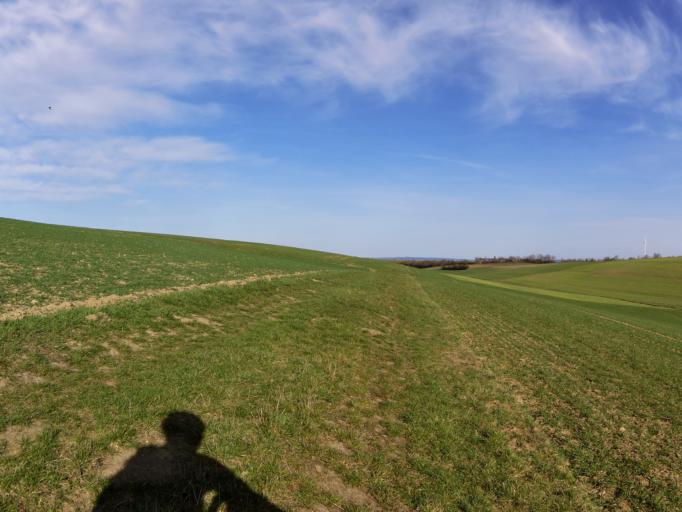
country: DE
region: Bavaria
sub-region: Regierungsbezirk Unterfranken
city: Biebelried
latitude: 49.7912
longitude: 10.0906
